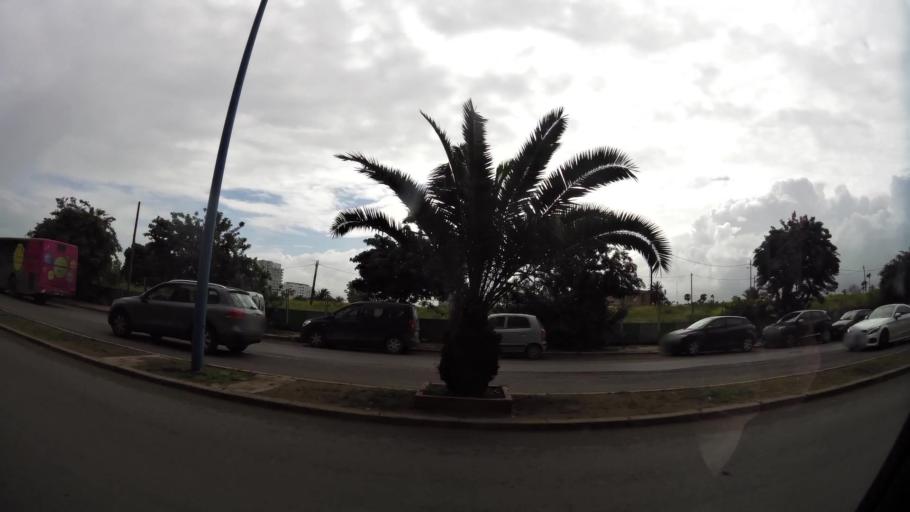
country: MA
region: Grand Casablanca
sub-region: Casablanca
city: Casablanca
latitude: 33.5641
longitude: -7.6681
